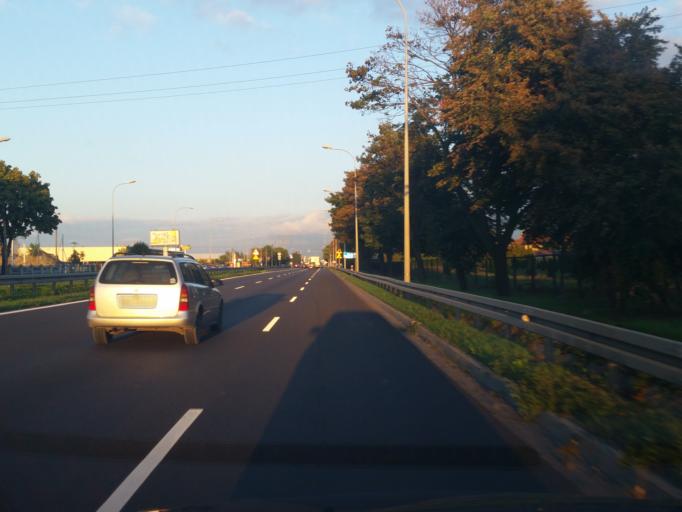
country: PL
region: Masovian Voivodeship
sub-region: Powiat pruszkowski
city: Piastow
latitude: 52.2150
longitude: 20.8450
